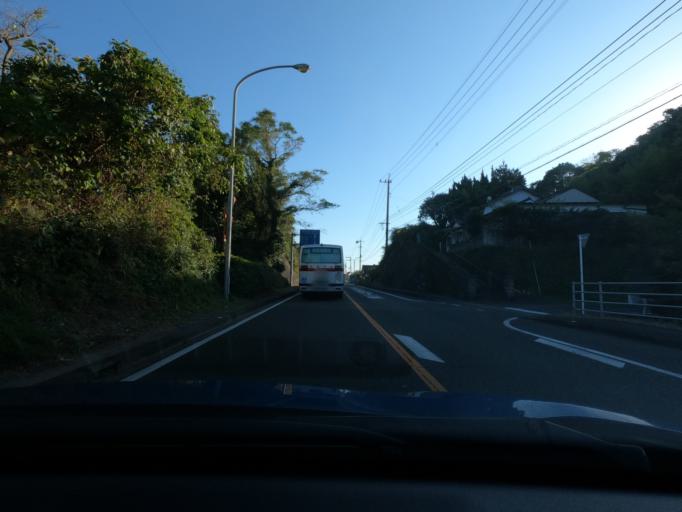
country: JP
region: Kagoshima
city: Akune
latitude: 31.9851
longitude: 130.2039
